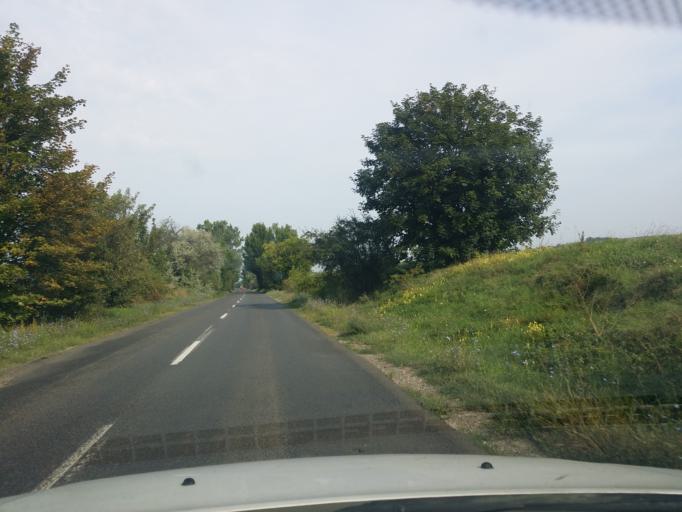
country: HU
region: Pest
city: Galgamacsa
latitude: 47.7073
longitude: 19.3913
